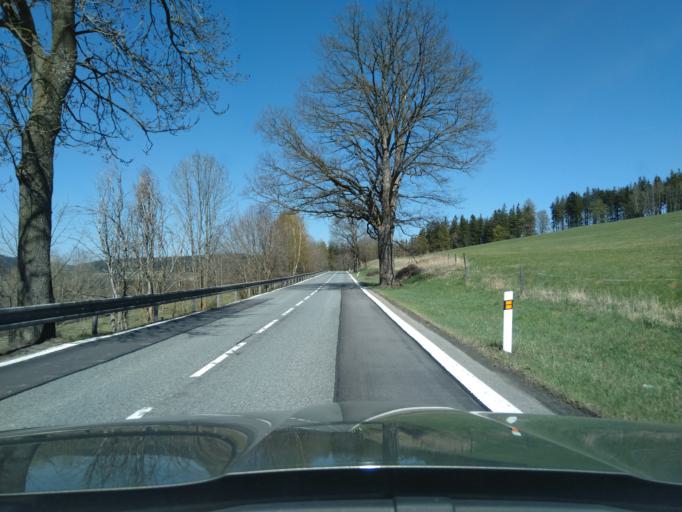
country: CZ
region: Jihocesky
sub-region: Okres Prachatice
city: Vimperk
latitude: 49.0328
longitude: 13.7625
